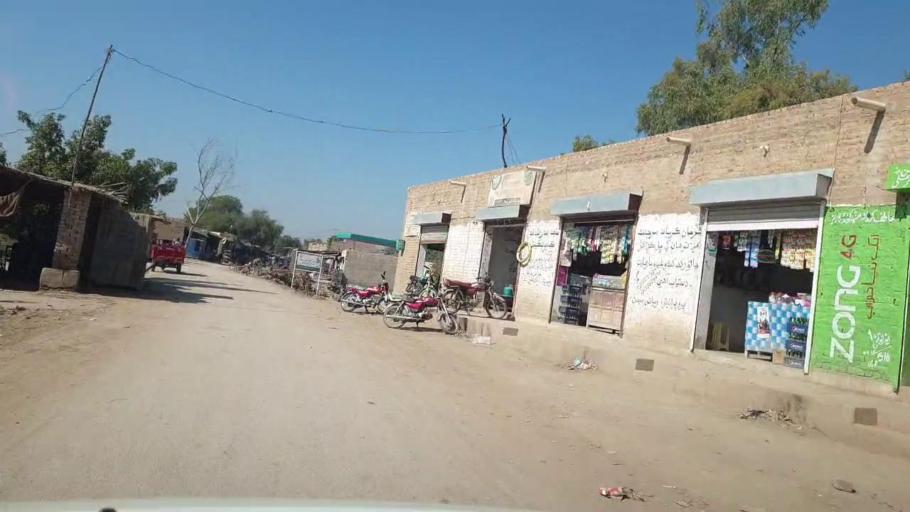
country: PK
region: Sindh
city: Bhan
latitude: 26.6493
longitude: 67.7133
